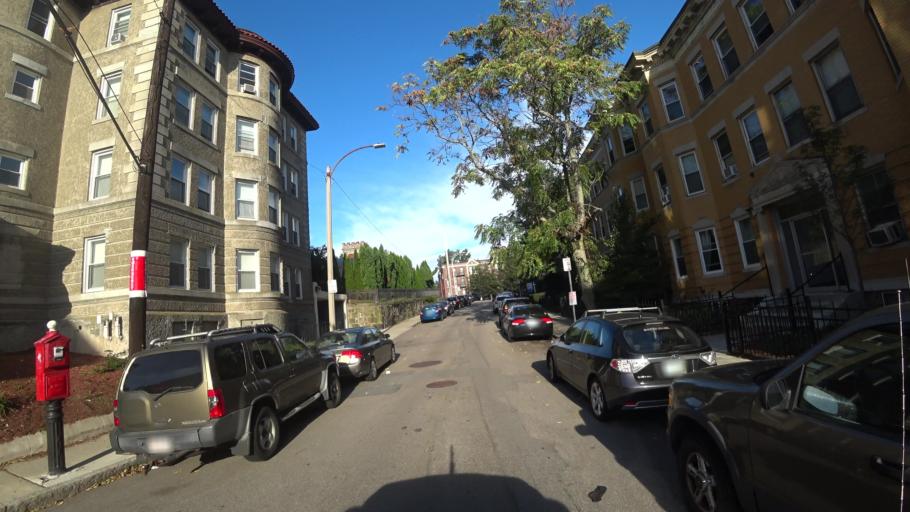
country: US
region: Massachusetts
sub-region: Norfolk County
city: Brookline
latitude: 42.3409
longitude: -71.1539
